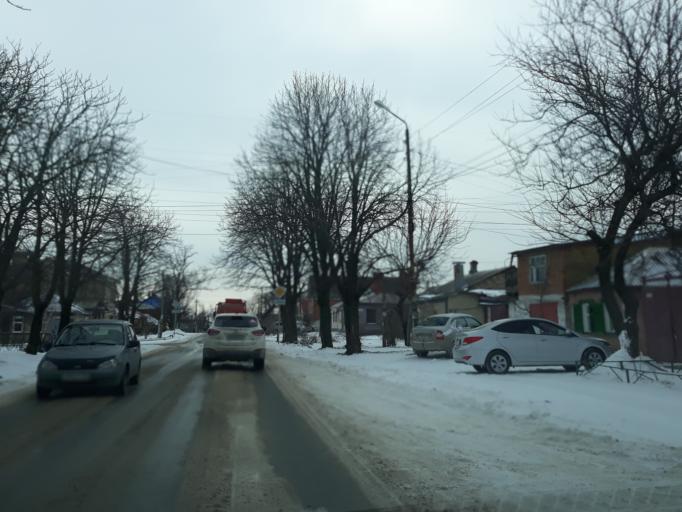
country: RU
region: Rostov
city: Taganrog
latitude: 47.2028
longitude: 38.9188
